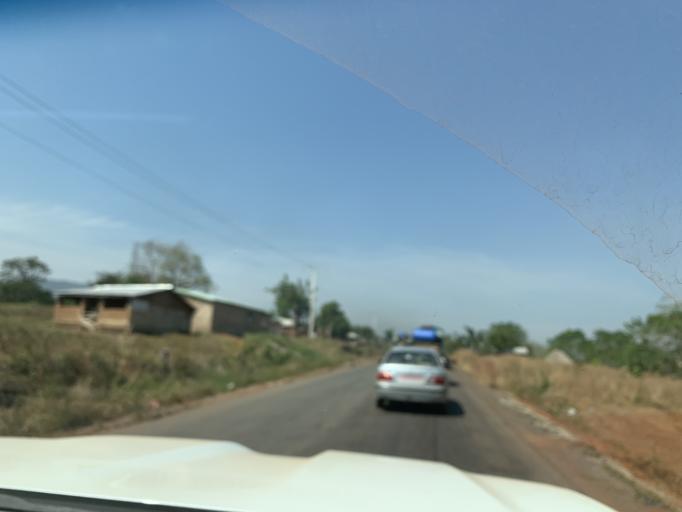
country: GN
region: Mamou
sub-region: Mamou Prefecture
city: Mamou
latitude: 10.1896
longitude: -12.4579
